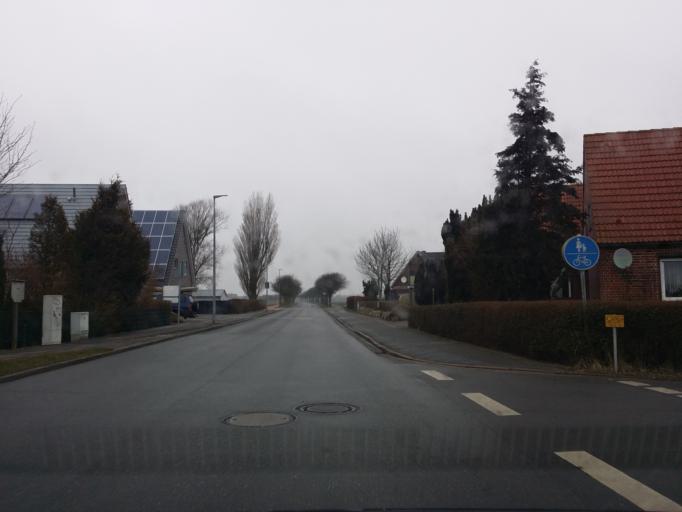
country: DE
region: Schleswig-Holstein
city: Burg auf Fehmarn
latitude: 54.4228
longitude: 11.2071
